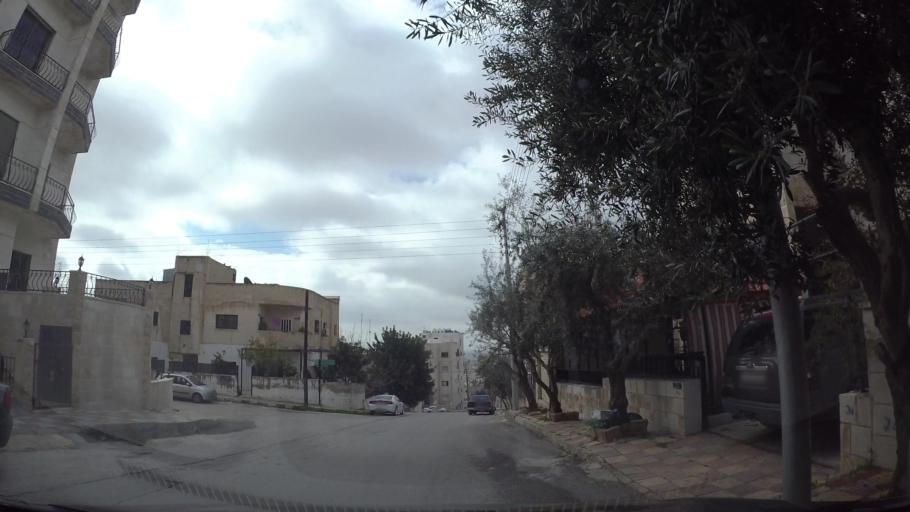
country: JO
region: Amman
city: Wadi as Sir
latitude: 31.9483
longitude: 35.8252
